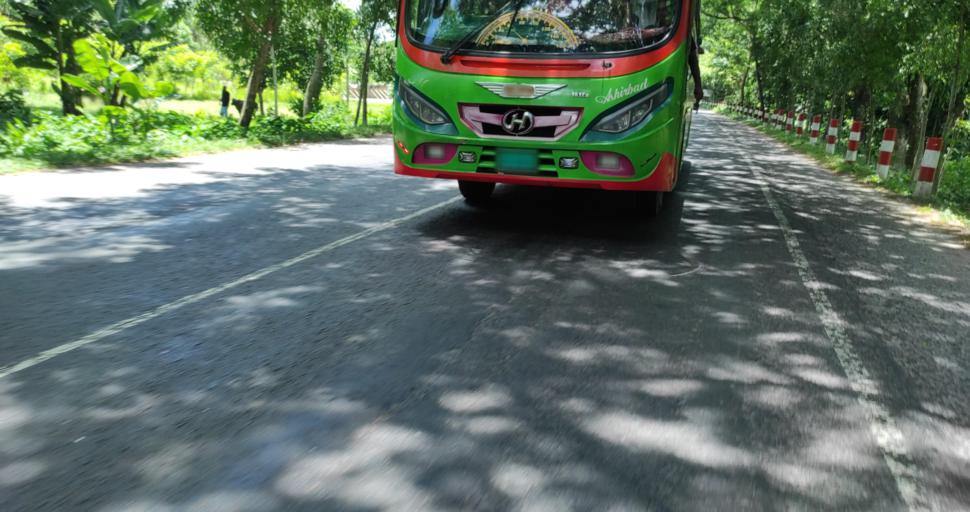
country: BD
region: Barisal
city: Gaurnadi
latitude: 22.8414
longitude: 90.2513
